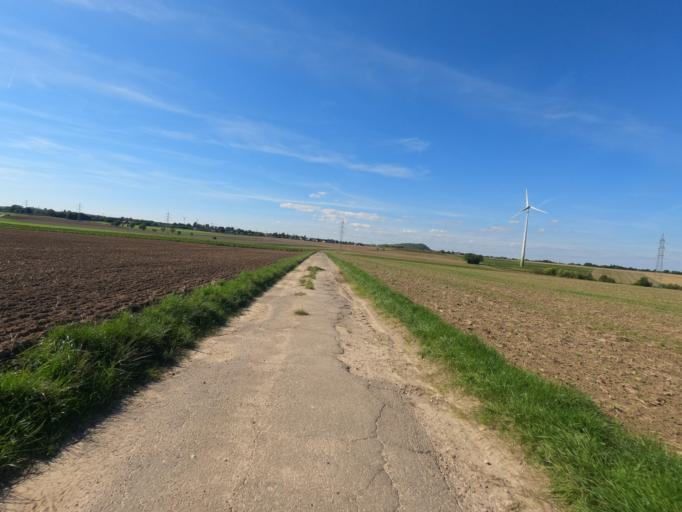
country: DE
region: North Rhine-Westphalia
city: Siersdorf
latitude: 50.8978
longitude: 6.2060
